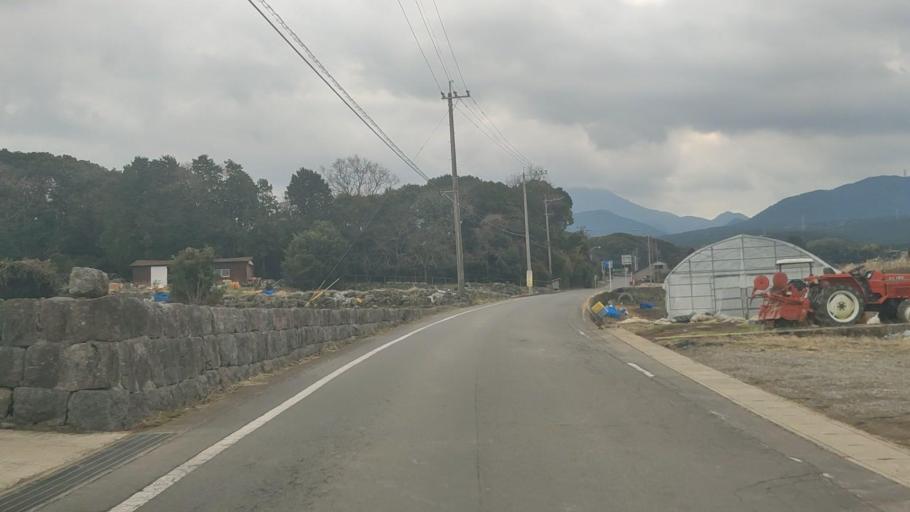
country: JP
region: Nagasaki
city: Shimabara
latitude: 32.8276
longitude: 130.2920
